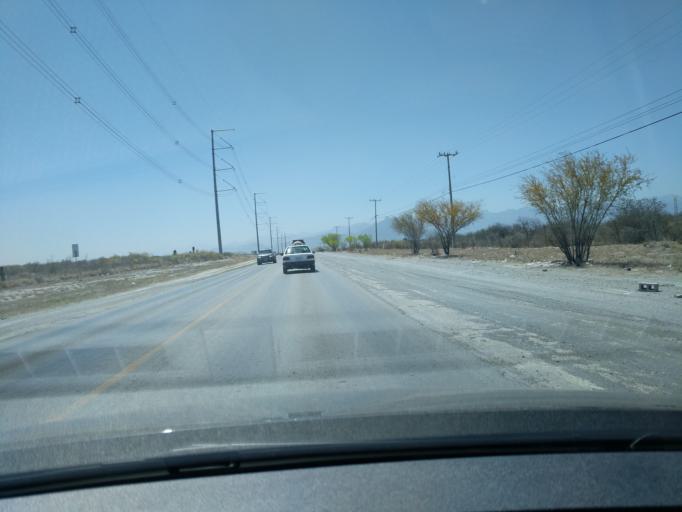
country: MX
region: Nuevo Leon
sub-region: Apodaca
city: Artemio Trevino
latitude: 25.8266
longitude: -100.1432
